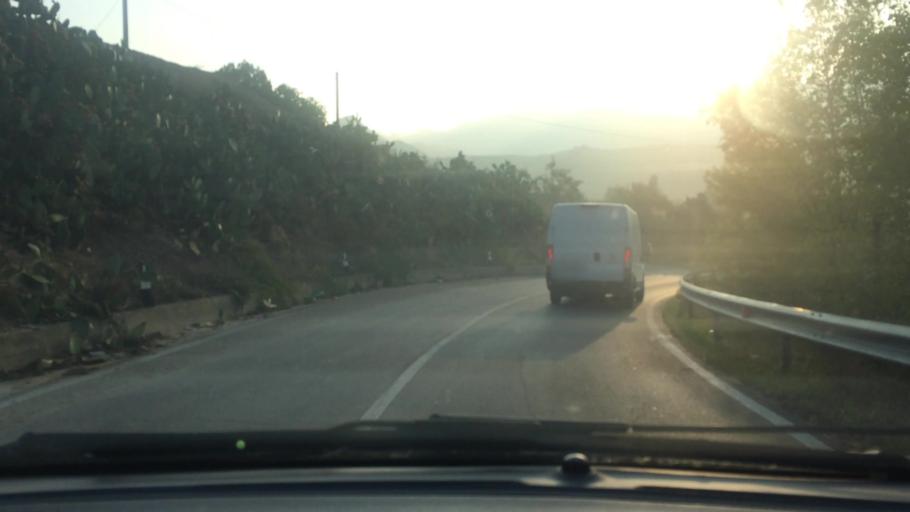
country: IT
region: Basilicate
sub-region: Provincia di Matera
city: Montescaglioso
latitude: 40.5356
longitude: 16.6435
